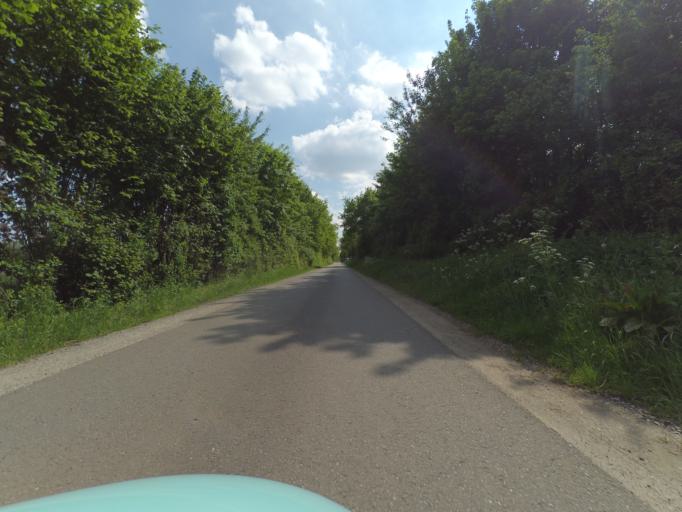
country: DE
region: Lower Saxony
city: Nienhagen
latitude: 52.5422
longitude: 10.0790
